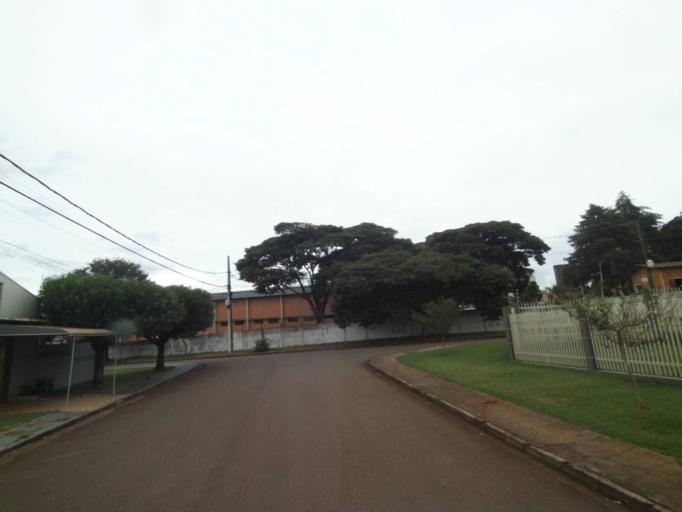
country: BR
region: Parana
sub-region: Campo Mourao
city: Campo Mourao
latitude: -24.0348
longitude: -52.3633
